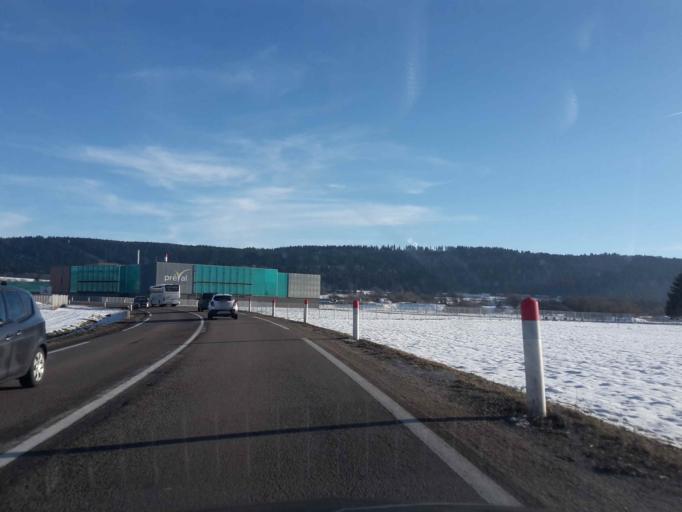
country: FR
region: Franche-Comte
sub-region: Departement du Doubs
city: Pontarlier
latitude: 46.9014
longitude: 6.3302
